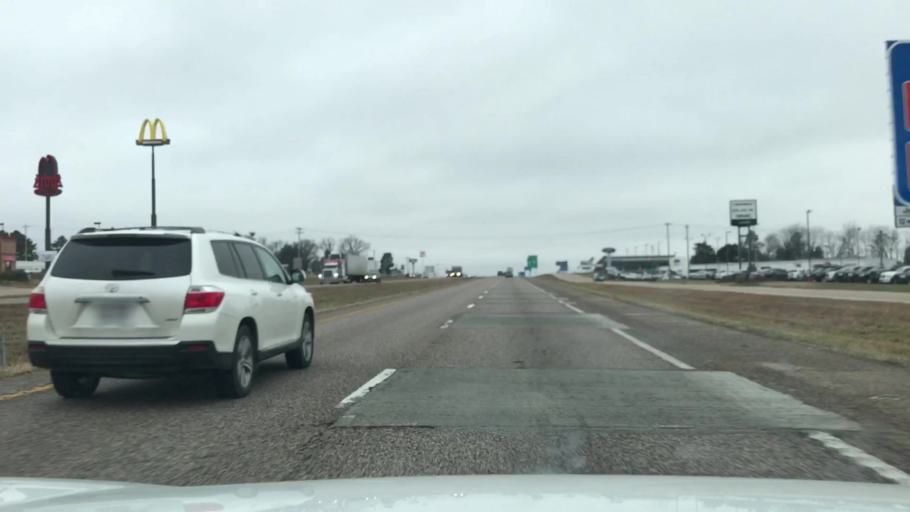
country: US
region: Missouri
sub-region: Franklin County
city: Sullivan
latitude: 38.2202
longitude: -91.1618
